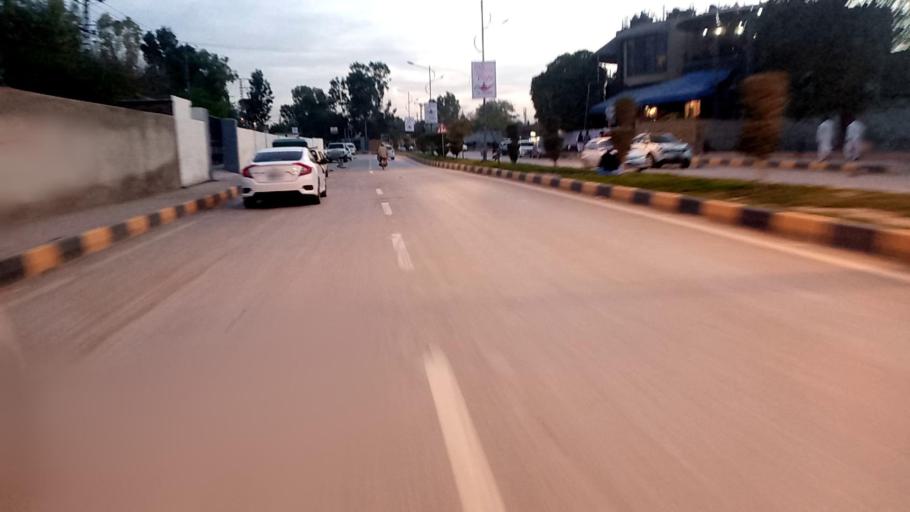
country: PK
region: Khyber Pakhtunkhwa
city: Peshawar
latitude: 34.0184
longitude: 71.5489
